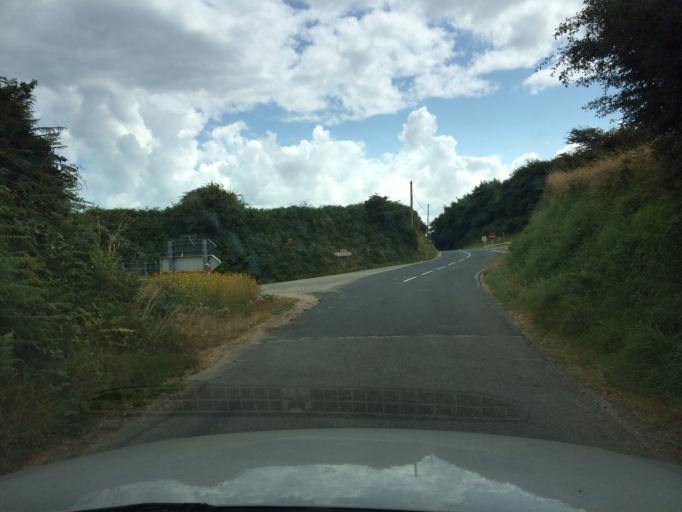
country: FR
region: Lower Normandy
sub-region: Departement de la Manche
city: Beaumont-Hague
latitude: 49.6827
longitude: -1.8576
